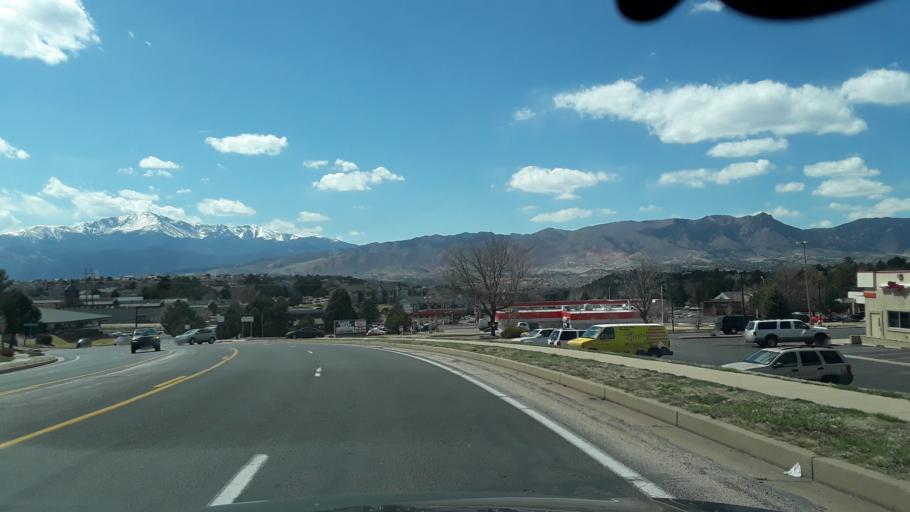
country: US
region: Colorado
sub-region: El Paso County
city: Colorado Springs
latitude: 38.9156
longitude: -104.7846
